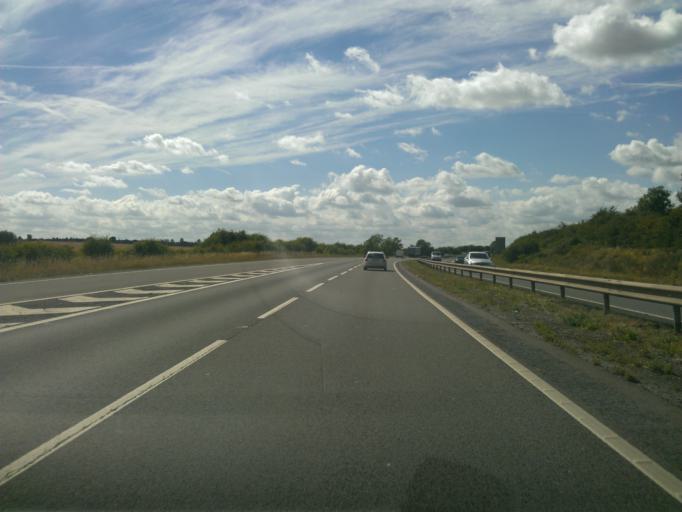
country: GB
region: England
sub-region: Northamptonshire
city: Thrapston
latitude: 52.3908
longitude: -0.5600
